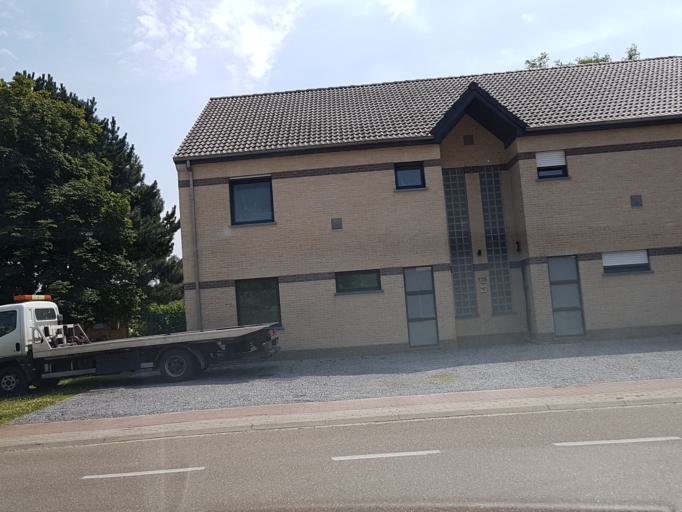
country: BE
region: Flanders
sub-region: Provincie Vlaams-Brabant
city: Boortmeerbeek
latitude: 50.9473
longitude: 4.6011
